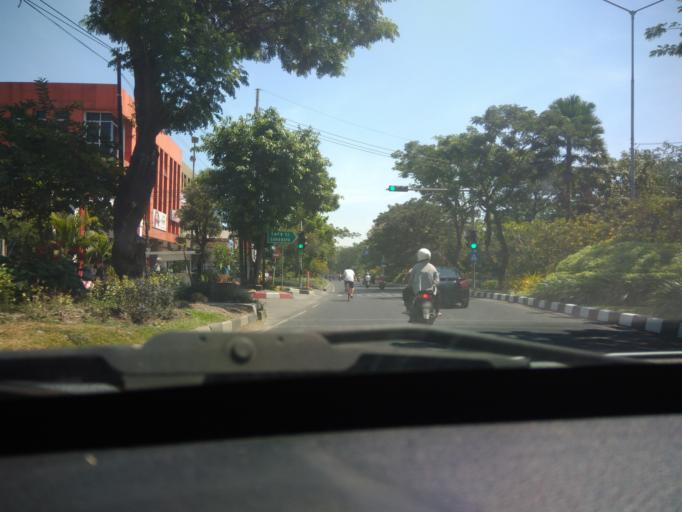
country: ID
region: East Java
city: Semampir
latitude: -7.3050
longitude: 112.7811
